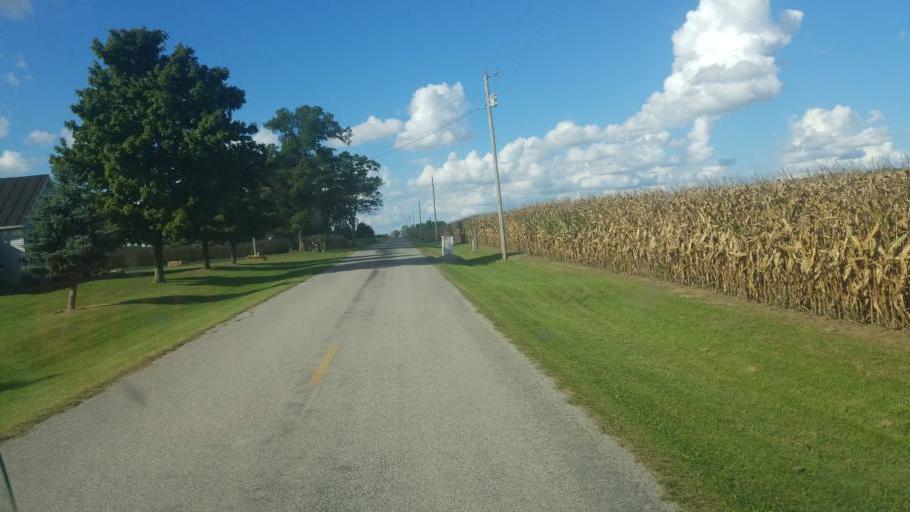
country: US
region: Ohio
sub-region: Hardin County
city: Kenton
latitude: 40.7072
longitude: -83.6919
